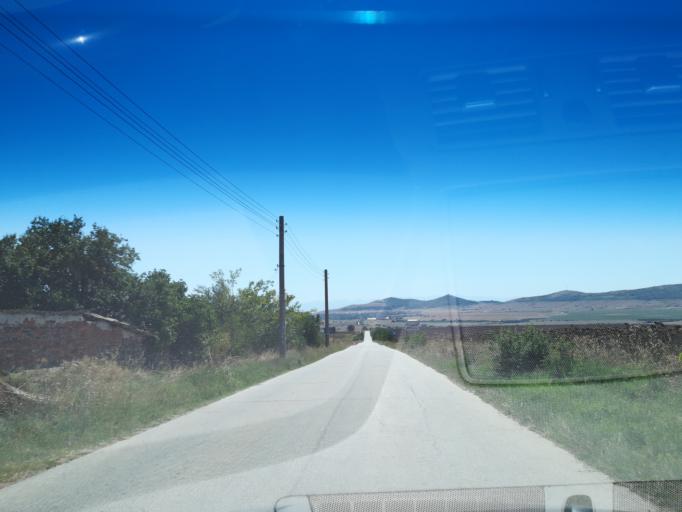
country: BG
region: Pazardzhik
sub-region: Obshtina Strelcha
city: Strelcha
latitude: 42.3706
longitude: 24.4026
